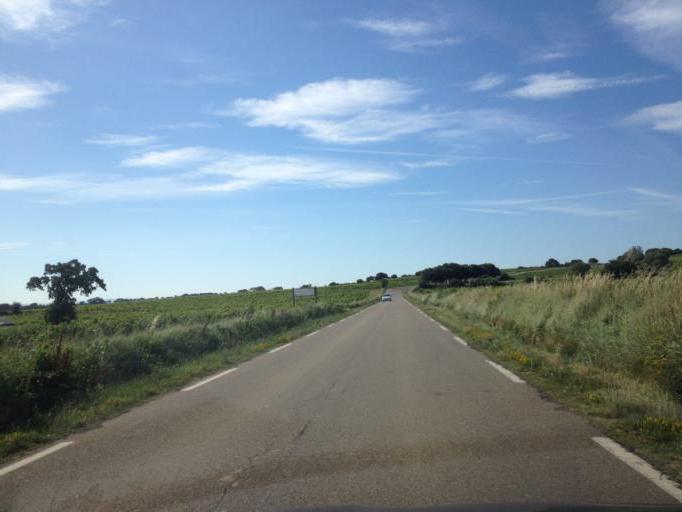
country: FR
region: Provence-Alpes-Cote d'Azur
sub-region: Departement du Vaucluse
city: Chateauneuf-du-Pape
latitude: 44.0894
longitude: 4.8286
